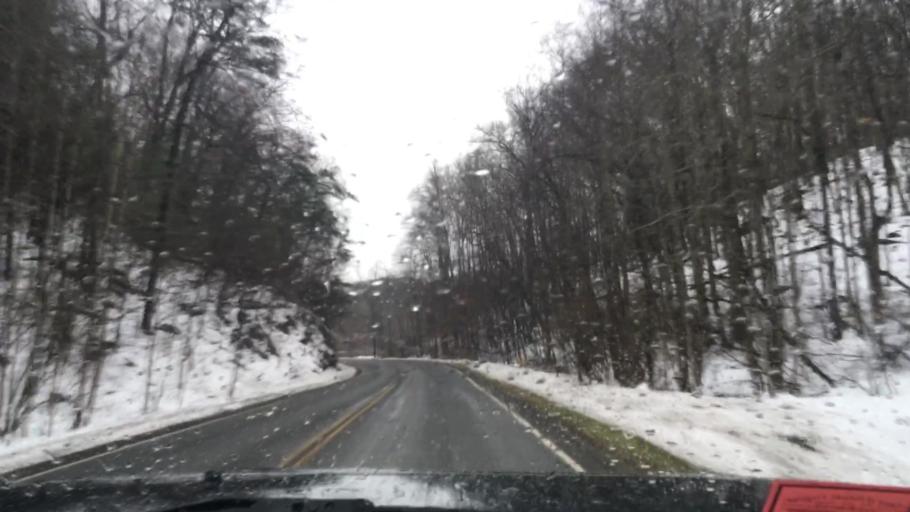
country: US
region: Virginia
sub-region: Pulaski County
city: Pulaski
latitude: 37.0186
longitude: -80.7076
